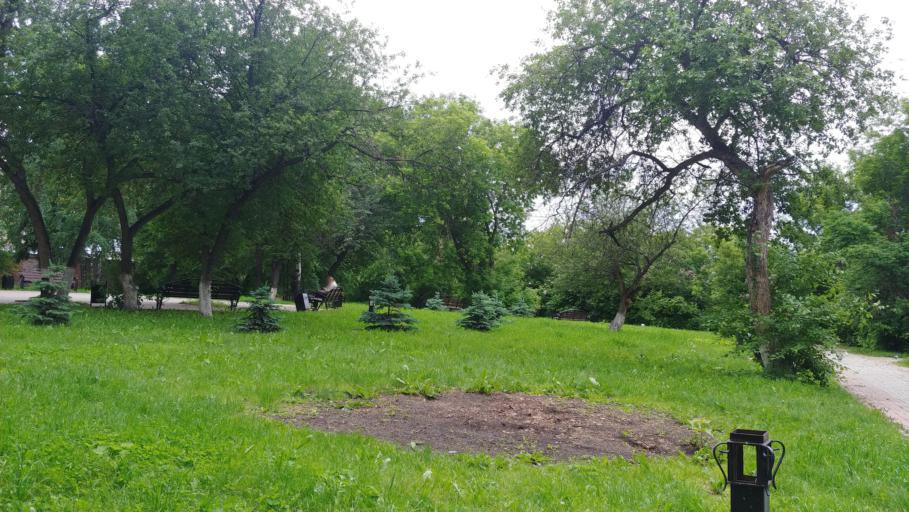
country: RU
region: Tomsk
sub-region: Tomskiy Rayon
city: Tomsk
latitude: 56.4757
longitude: 84.9494
